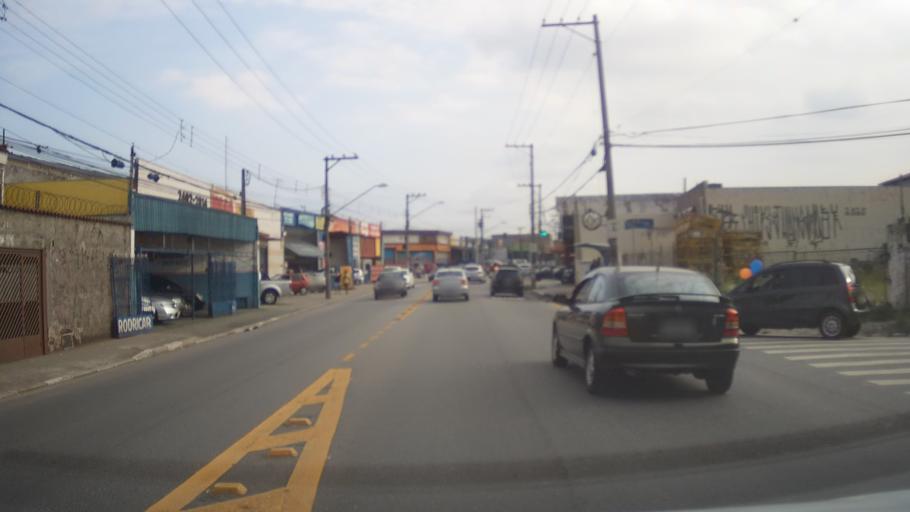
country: BR
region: Sao Paulo
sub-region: Guarulhos
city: Guarulhos
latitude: -23.4427
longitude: -46.5077
